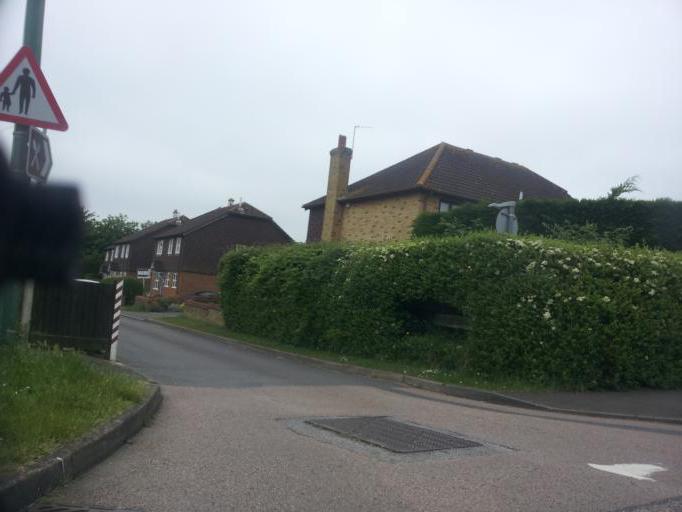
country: GB
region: England
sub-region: Kent
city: Boxley
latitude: 51.2760
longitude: 0.5596
